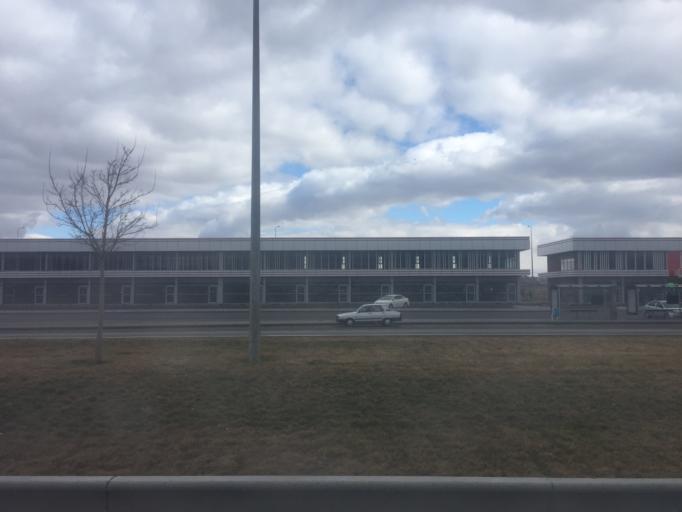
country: TR
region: Kayseri
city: Melikgazi
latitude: 38.7712
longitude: 35.4126
